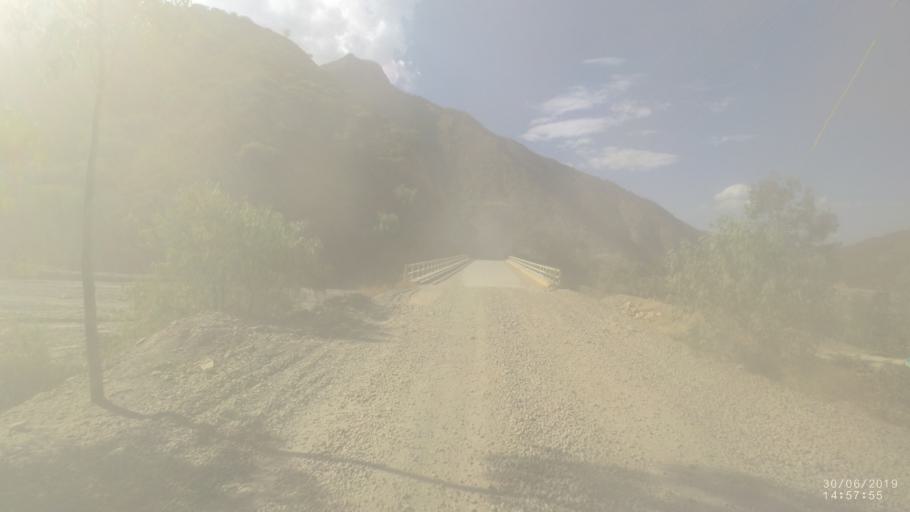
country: BO
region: Cochabamba
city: Irpa Irpa
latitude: -17.7416
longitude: -66.3518
